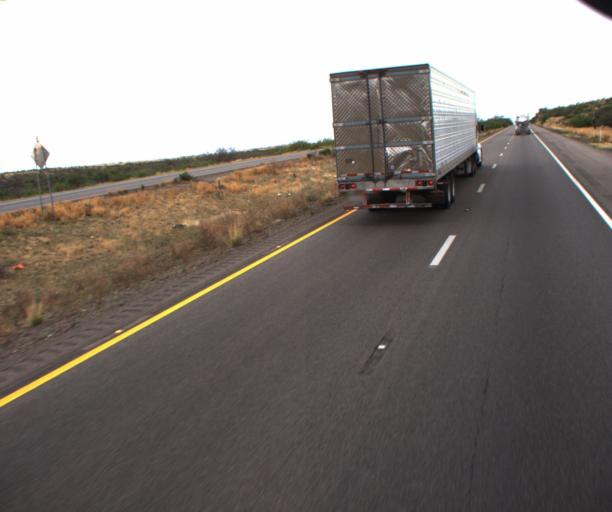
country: US
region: Arizona
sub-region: Cochise County
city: Saint David
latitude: 32.0107
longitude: -110.1275
